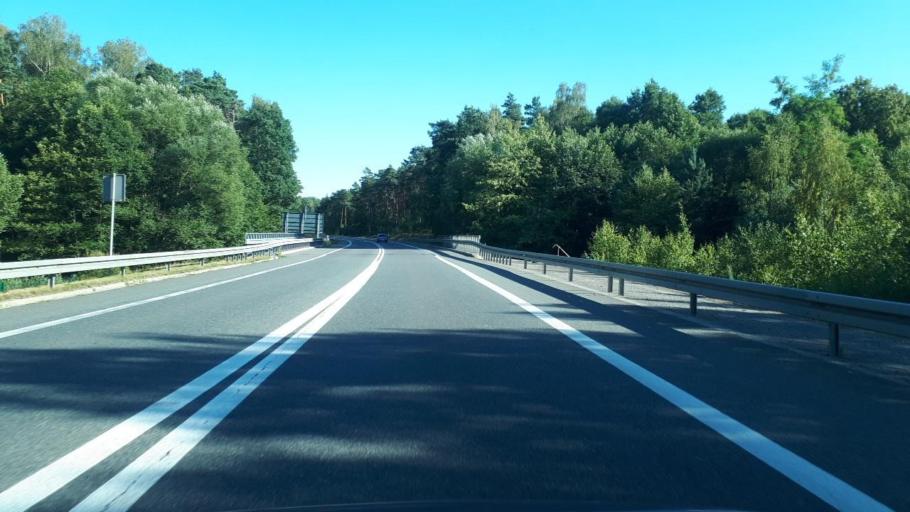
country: PL
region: Silesian Voivodeship
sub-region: Powiat lubliniecki
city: Lubliniec
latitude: 50.6625
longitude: 18.6534
